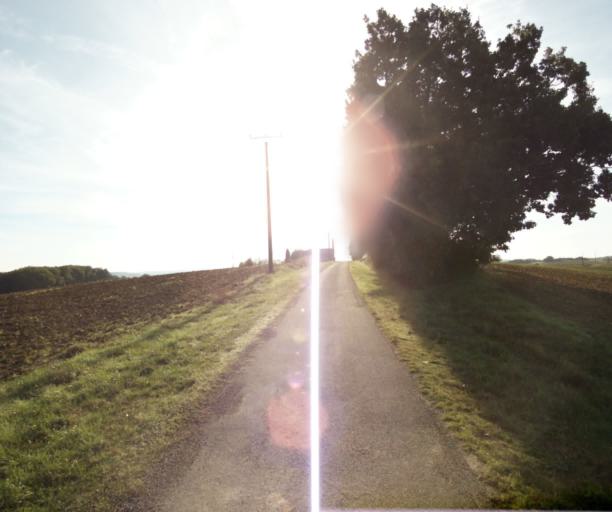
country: FR
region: Midi-Pyrenees
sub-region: Departement de la Haute-Garonne
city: Villemur-sur-Tarn
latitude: 43.9247
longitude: 1.4903
